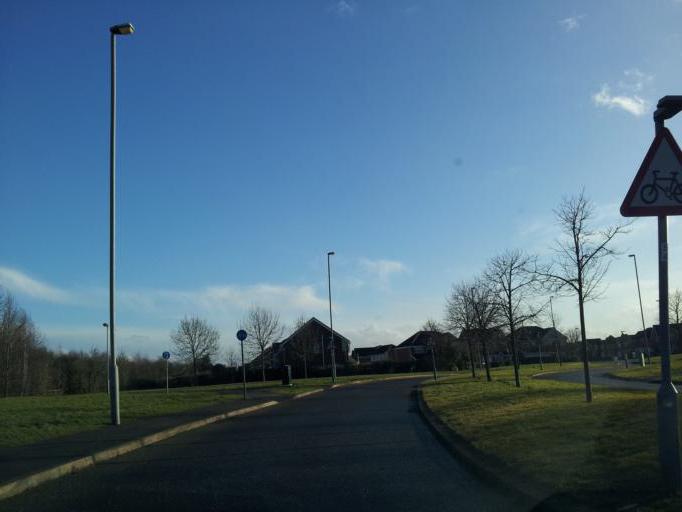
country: GB
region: England
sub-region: Nottinghamshire
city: Newark on Trent
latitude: 53.0766
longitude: -0.7715
